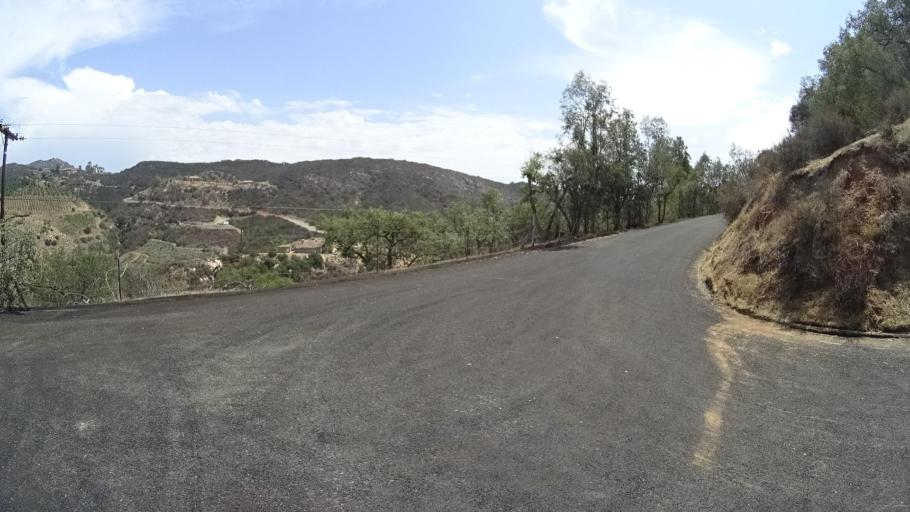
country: US
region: California
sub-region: San Diego County
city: Hidden Meadows
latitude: 33.1925
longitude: -117.0859
